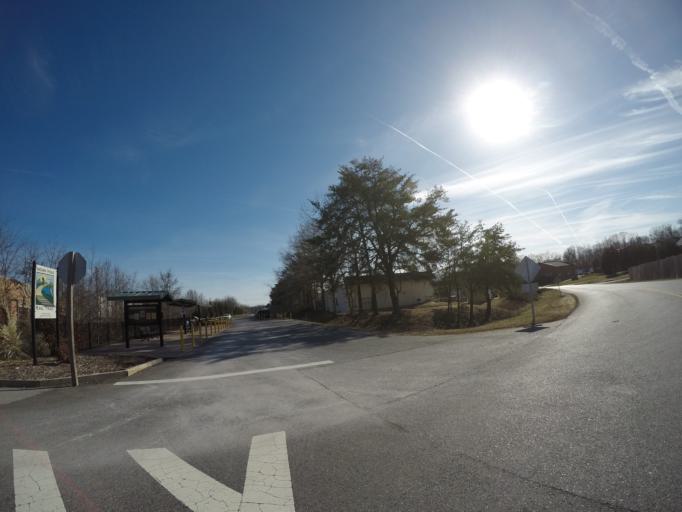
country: US
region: Maryland
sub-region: Charles County
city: Saint Charles
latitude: 38.5920
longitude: -76.9475
